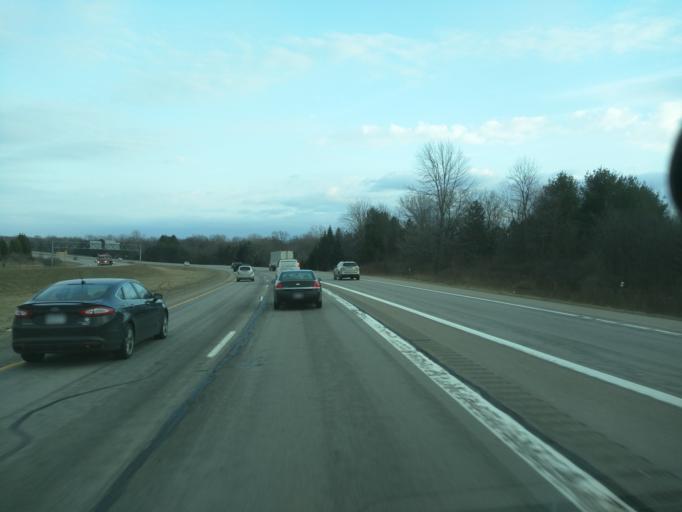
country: US
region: Michigan
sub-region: Ingham County
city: Holt
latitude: 42.6716
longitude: -84.4932
